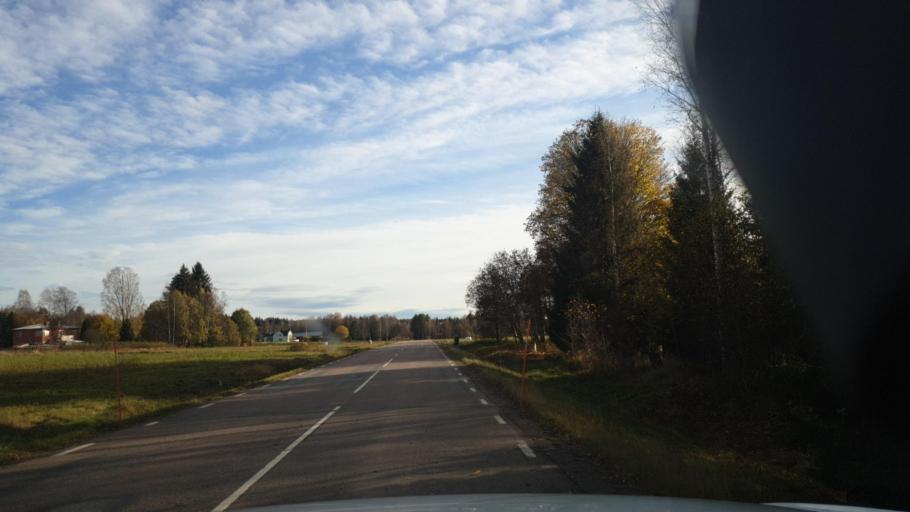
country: SE
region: Vaermland
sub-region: Eda Kommun
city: Charlottenberg
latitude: 59.9163
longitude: 12.2873
